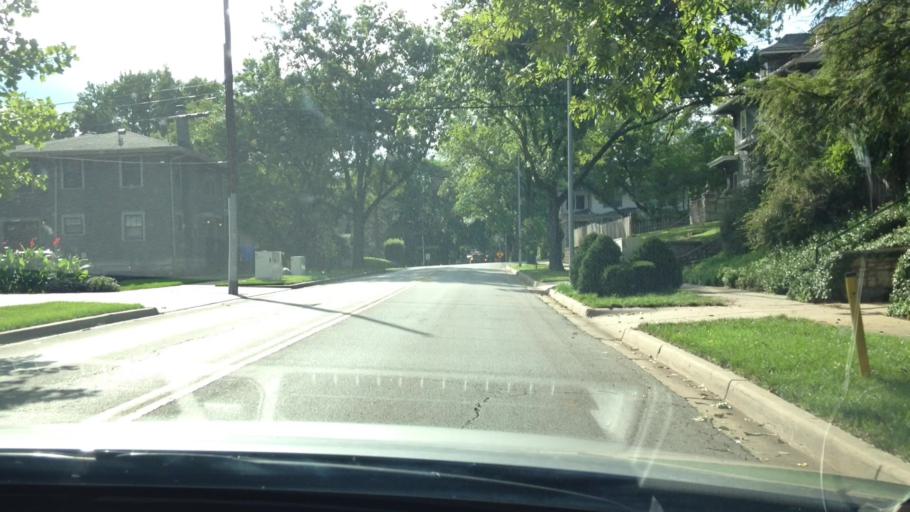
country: US
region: Kansas
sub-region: Johnson County
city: Mission Hills
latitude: 39.0206
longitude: -94.5906
